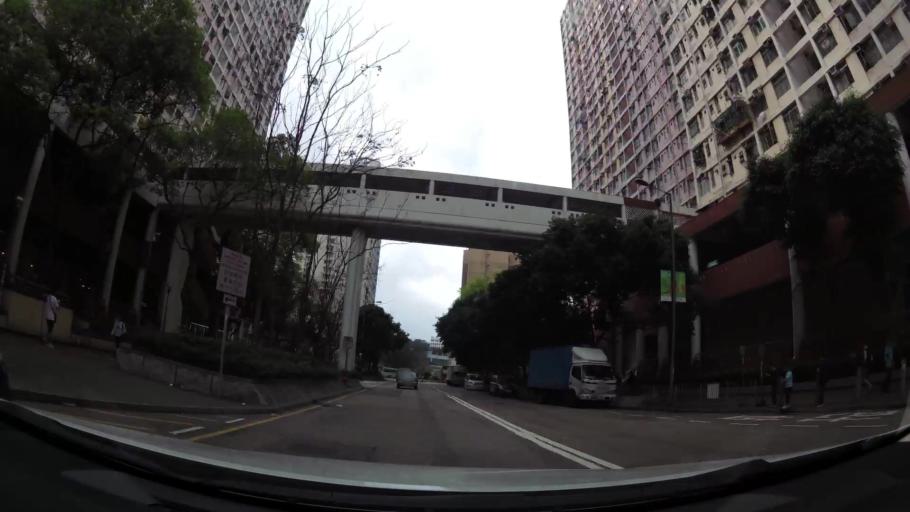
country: HK
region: Kowloon City
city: Kowloon
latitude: 22.3143
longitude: 114.2296
